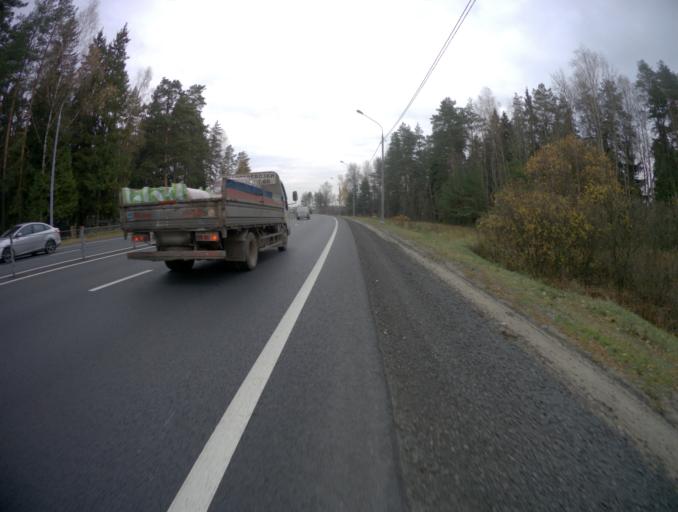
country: RU
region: Moskovskaya
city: Malaya Dubna
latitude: 55.8683
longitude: 38.9642
